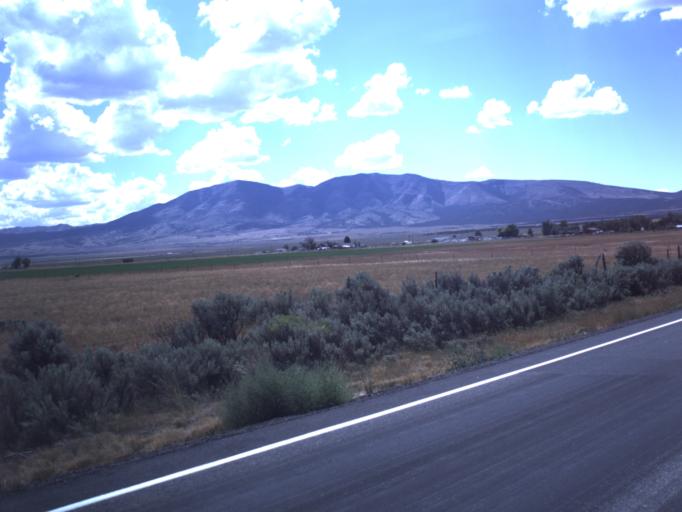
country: US
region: Utah
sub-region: Tooele County
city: Tooele
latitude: 40.3369
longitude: -112.4264
